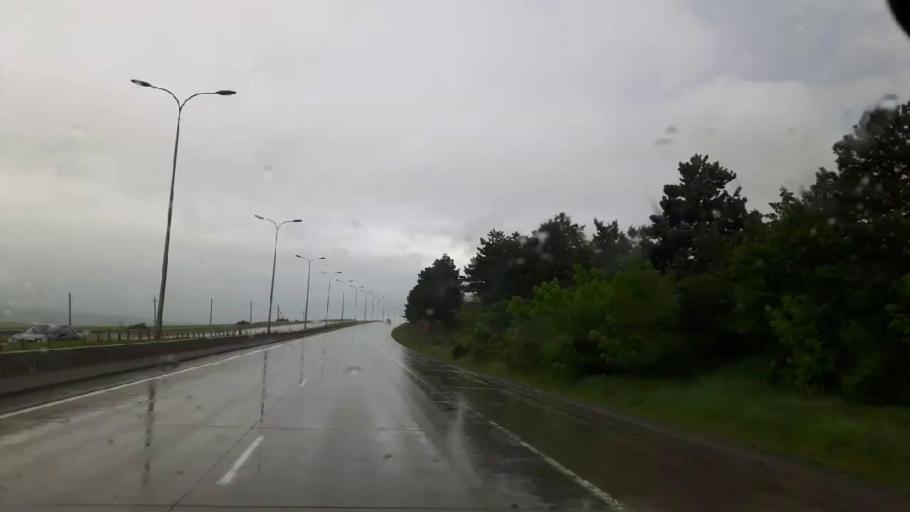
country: GE
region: Shida Kartli
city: Gori
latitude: 42.0250
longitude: 44.2137
